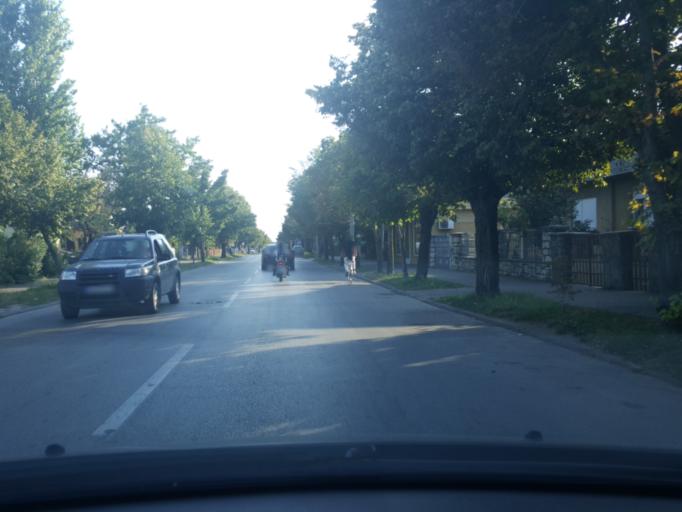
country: RS
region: Central Serbia
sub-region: Macvanski Okrug
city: Sabac
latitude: 44.7476
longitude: 19.7022
